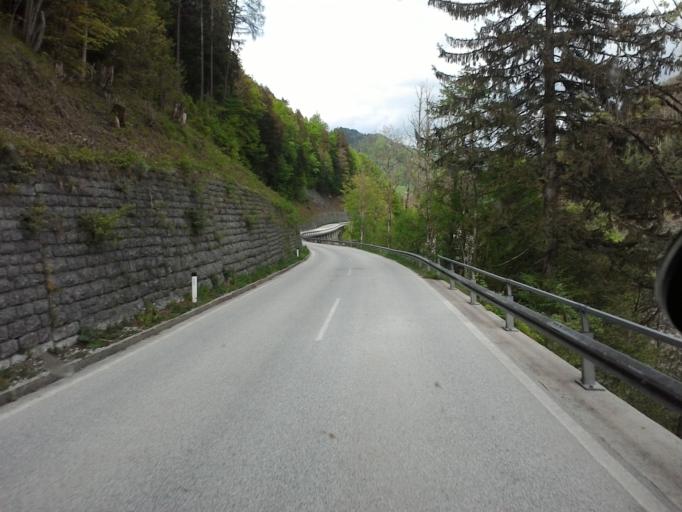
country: AT
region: Styria
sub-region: Politischer Bezirk Liezen
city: Landl
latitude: 47.6684
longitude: 14.7181
